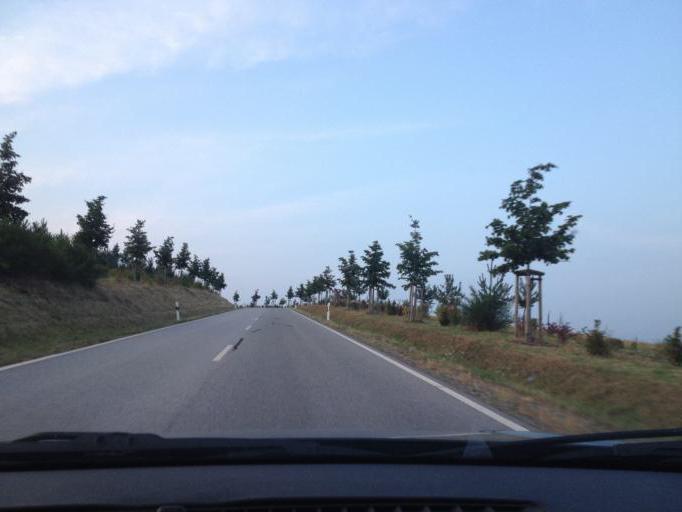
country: DE
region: Rheinland-Pfalz
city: Achtelsbach
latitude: 49.5728
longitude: 7.0855
